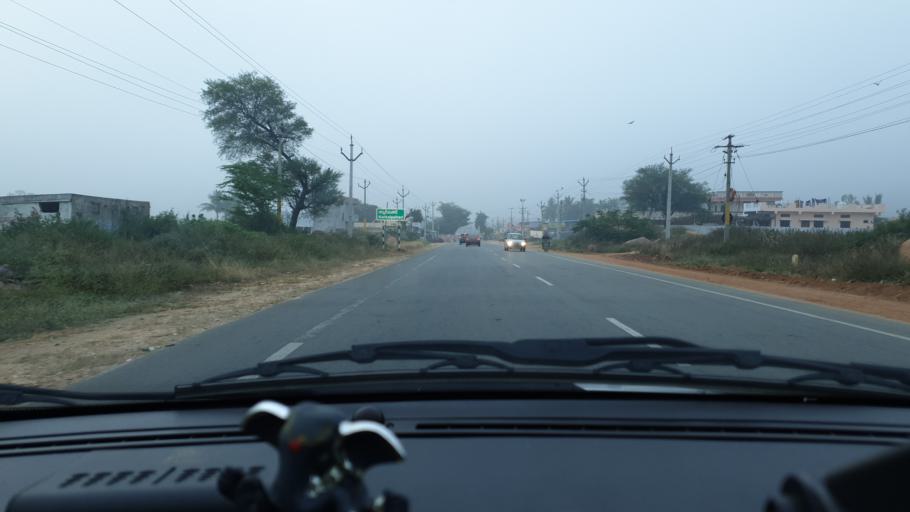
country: IN
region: Telangana
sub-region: Mahbubnagar
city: Farrukhnagar
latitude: 16.9273
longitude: 78.5276
